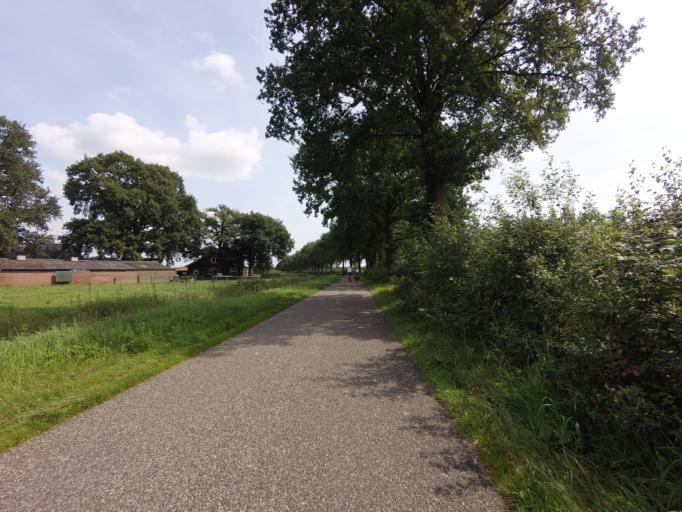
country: DE
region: Lower Saxony
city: Lage
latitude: 52.3952
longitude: 6.9356
